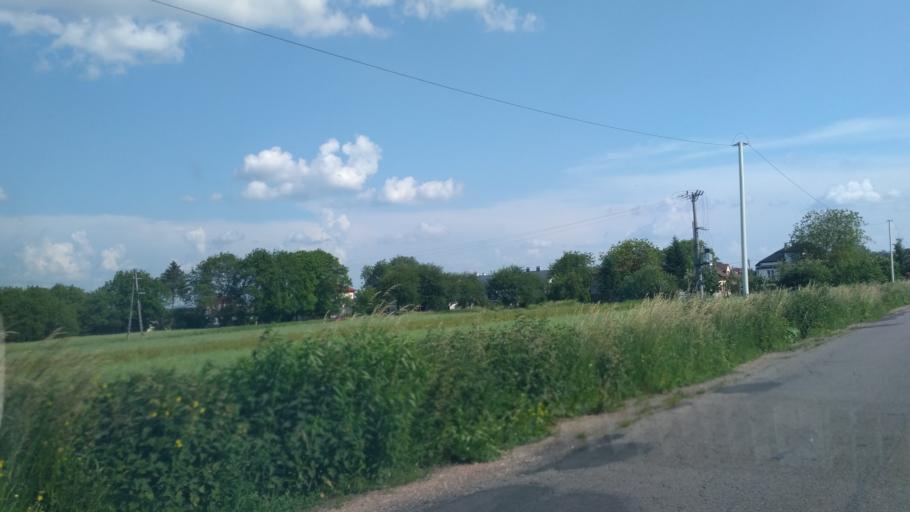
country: PL
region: Subcarpathian Voivodeship
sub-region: Powiat jaroslawski
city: Ostrow
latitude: 49.9305
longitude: 22.7409
